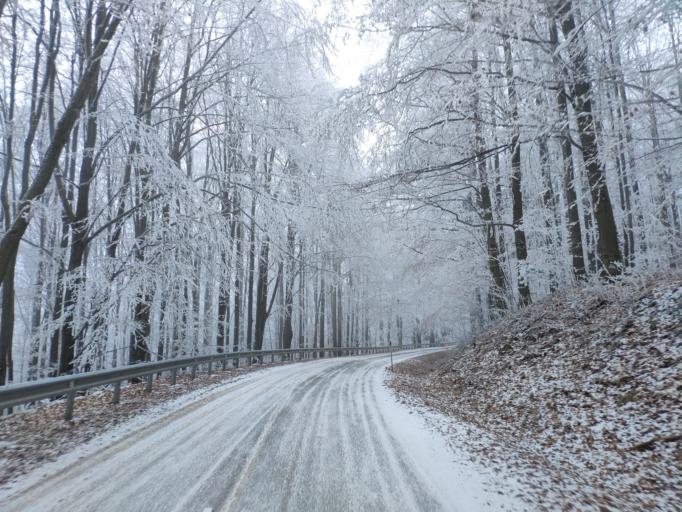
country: SK
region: Kosicky
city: Dobsina
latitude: 48.8082
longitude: 20.4827
